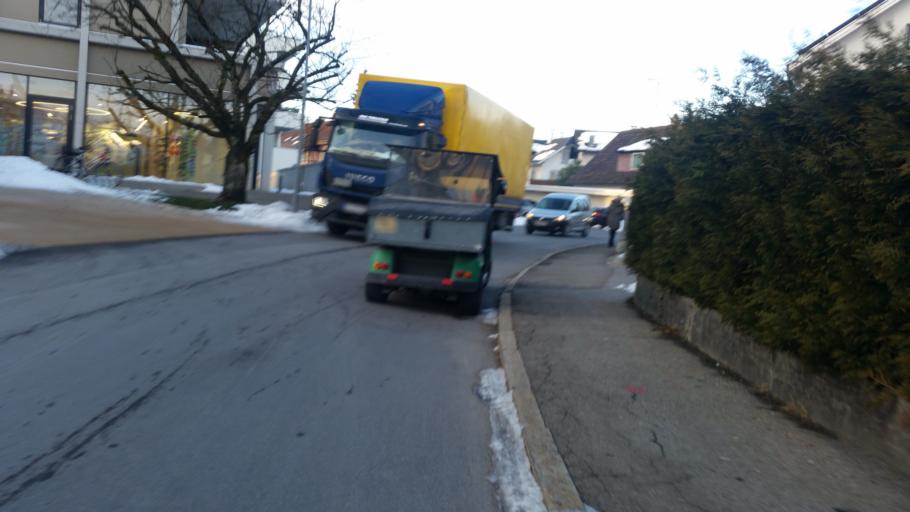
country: AT
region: Vorarlberg
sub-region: Politischer Bezirk Bregenz
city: Hard
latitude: 47.4894
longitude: 9.6929
